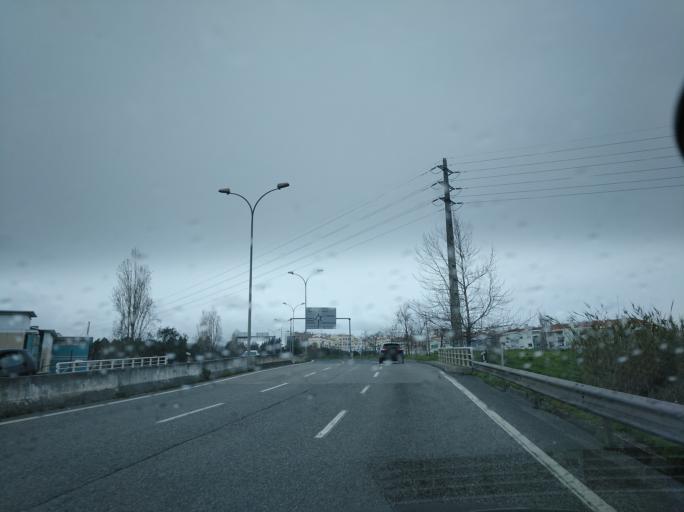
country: PT
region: Lisbon
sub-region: Odivelas
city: Odivelas
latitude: 38.7818
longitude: -9.1899
